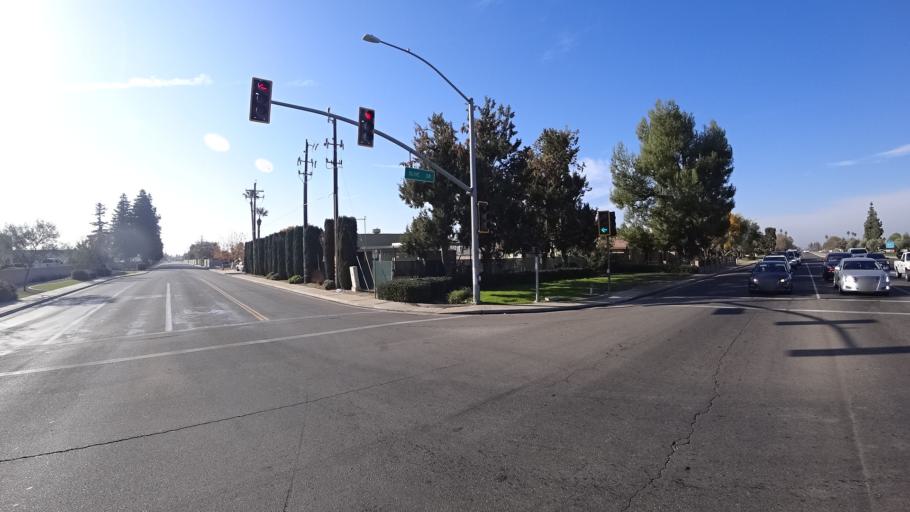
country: US
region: California
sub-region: Kern County
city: Oildale
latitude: 35.4123
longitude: -119.0622
